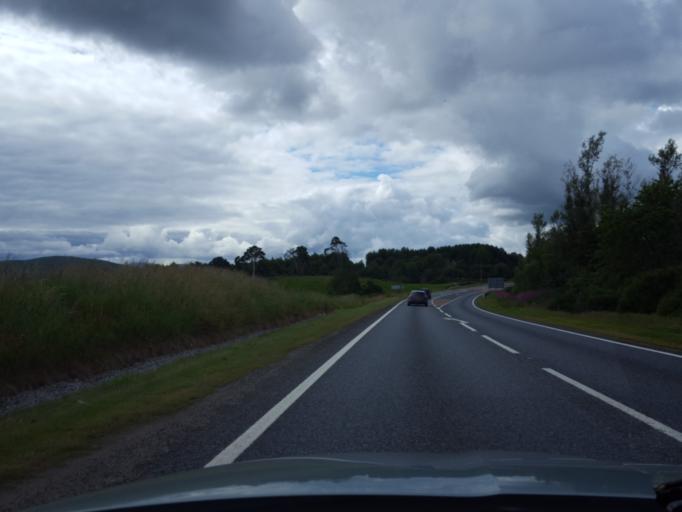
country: GB
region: Scotland
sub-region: Highland
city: Grantown on Spey
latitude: 57.3183
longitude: -3.6211
